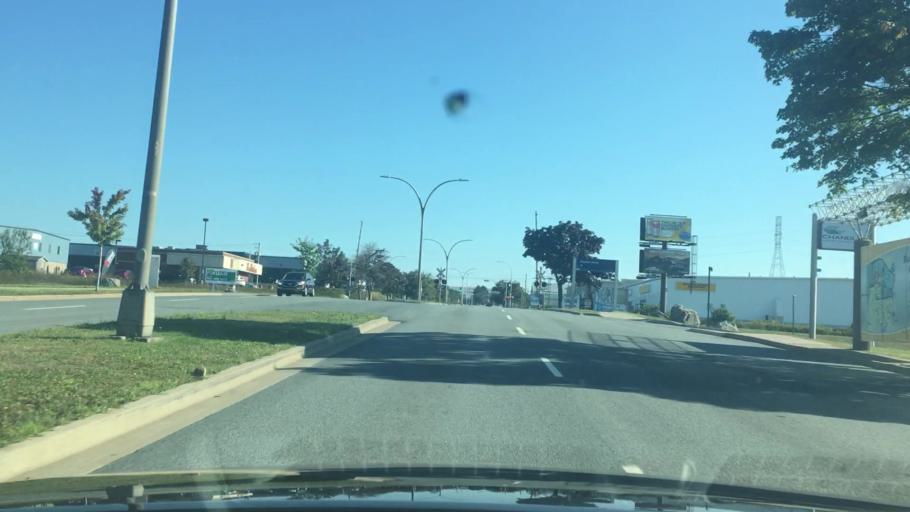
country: CA
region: Nova Scotia
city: Dartmouth
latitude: 44.7062
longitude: -63.6091
